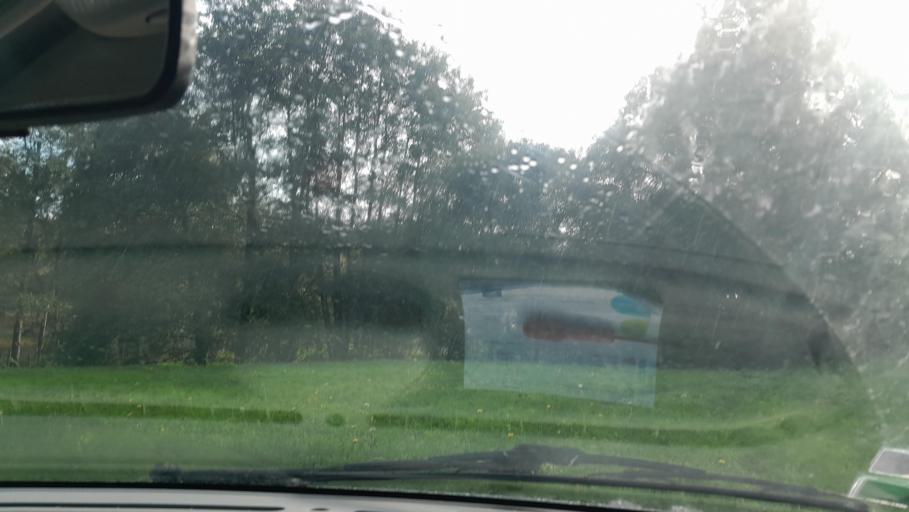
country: FR
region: Pays de la Loire
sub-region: Departement de la Mayenne
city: Cosse-le-Vivien
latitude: 47.9358
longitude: -0.8969
